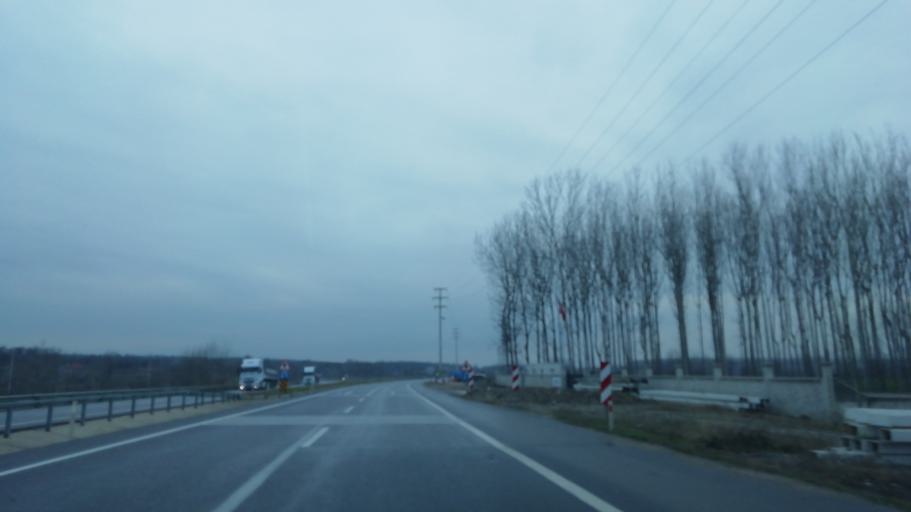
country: TR
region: Sakarya
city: Akyazi
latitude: 40.6476
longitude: 30.6082
